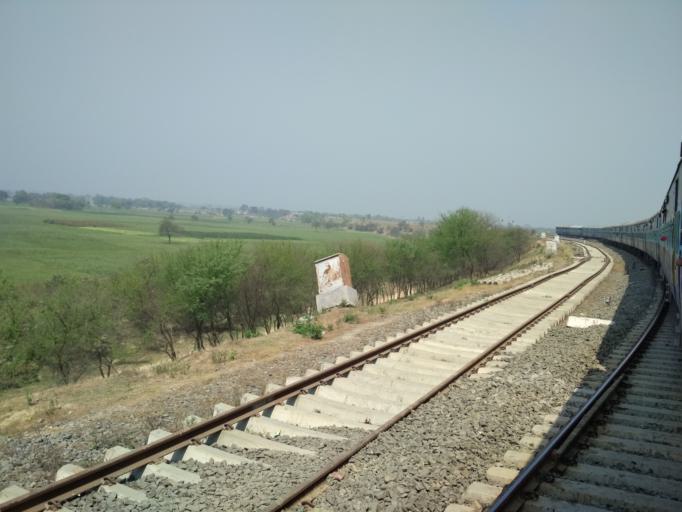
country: IN
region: Bihar
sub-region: Munger
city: Munger
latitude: 25.4312
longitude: 86.4390
